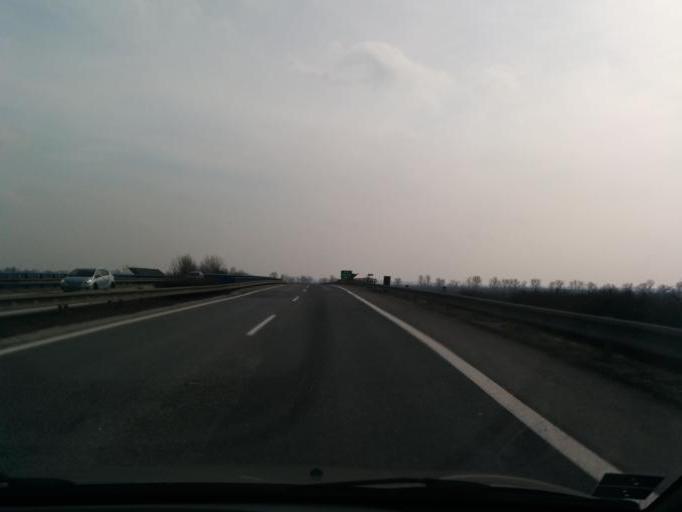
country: SK
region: Trnavsky
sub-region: Okres Galanta
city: Galanta
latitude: 48.2645
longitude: 17.7274
